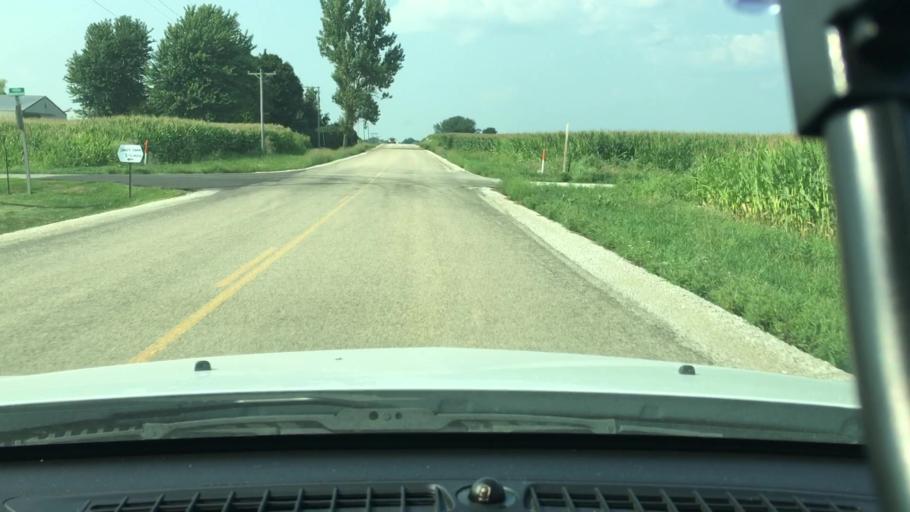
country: US
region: Illinois
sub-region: DeKalb County
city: Waterman
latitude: 41.8343
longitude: -88.7733
